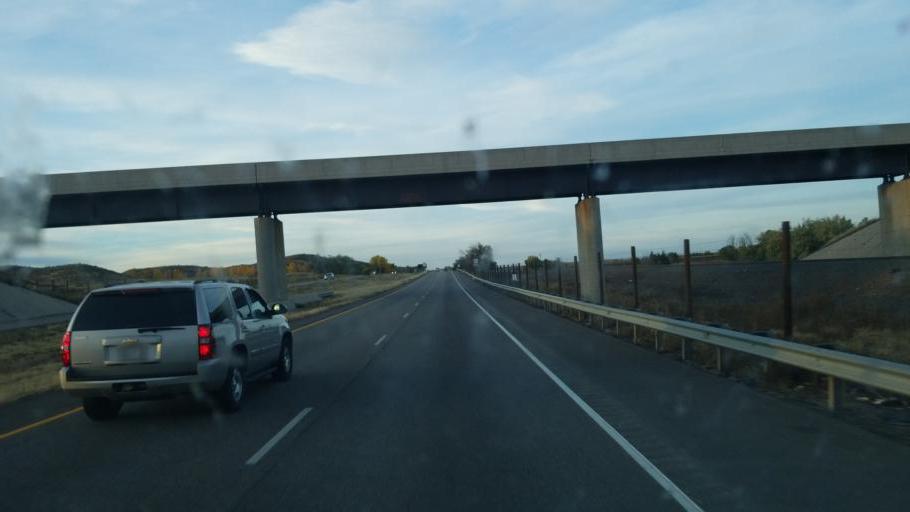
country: US
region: Colorado
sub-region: El Paso County
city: Fountain
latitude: 38.6328
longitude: -104.6914
